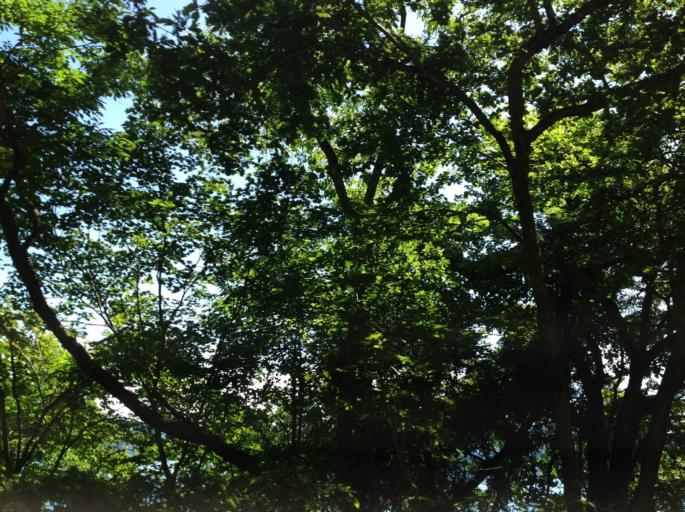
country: JP
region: Akita
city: Kakunodatemachi
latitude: 39.7072
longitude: 140.6395
